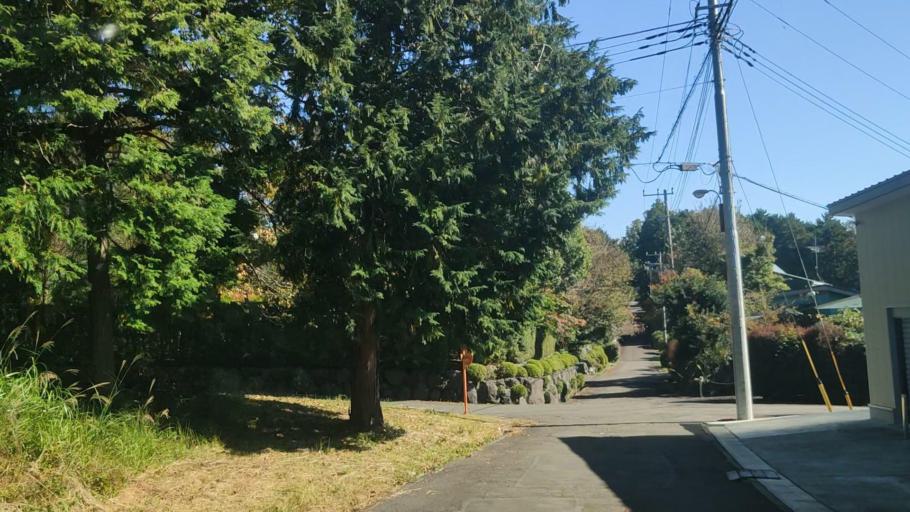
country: JP
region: Shizuoka
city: Ito
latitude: 34.9478
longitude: 139.0080
